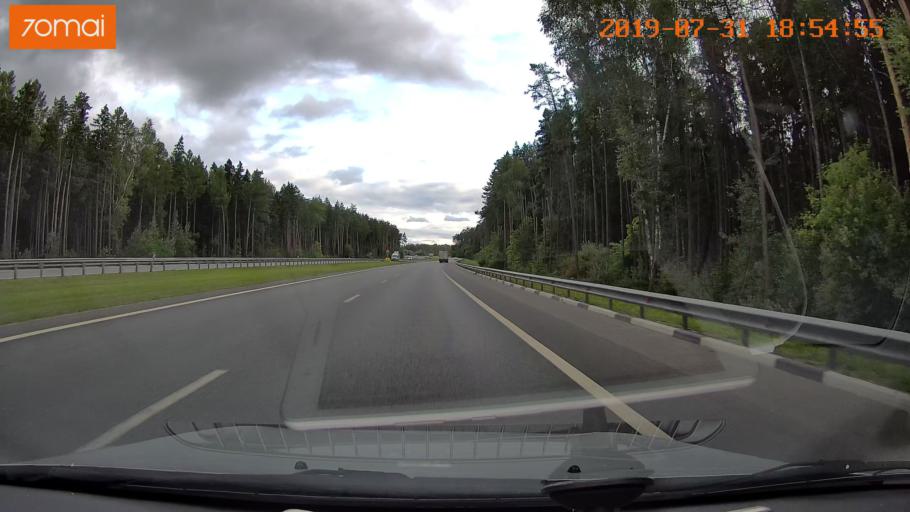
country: RU
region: Moskovskaya
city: Raduzhnyy
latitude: 55.1824
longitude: 38.6691
